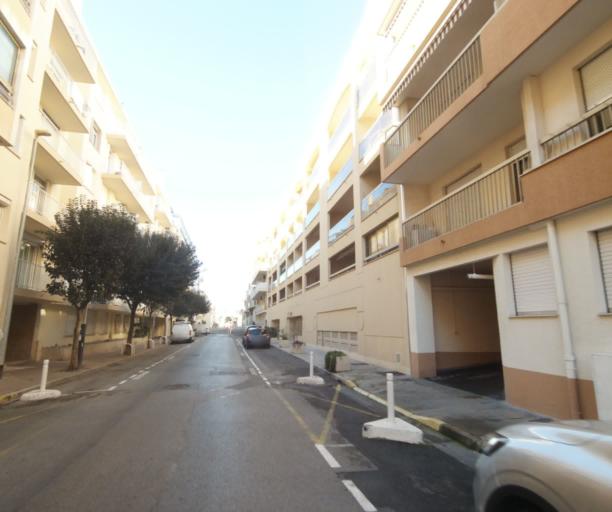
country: FR
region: Provence-Alpes-Cote d'Azur
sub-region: Departement des Alpes-Maritimes
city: Antibes
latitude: 43.5714
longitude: 7.1063
